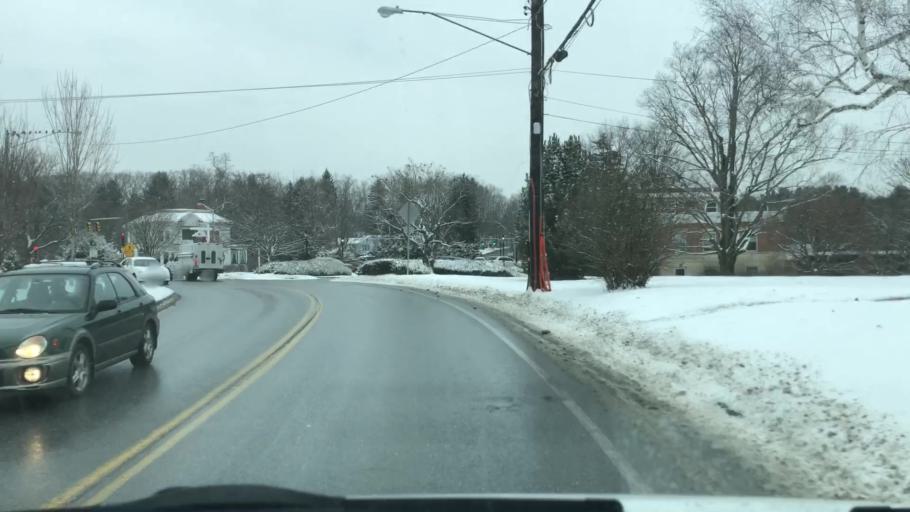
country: US
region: Massachusetts
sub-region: Berkshire County
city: Dalton
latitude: 42.4702
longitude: -73.1790
